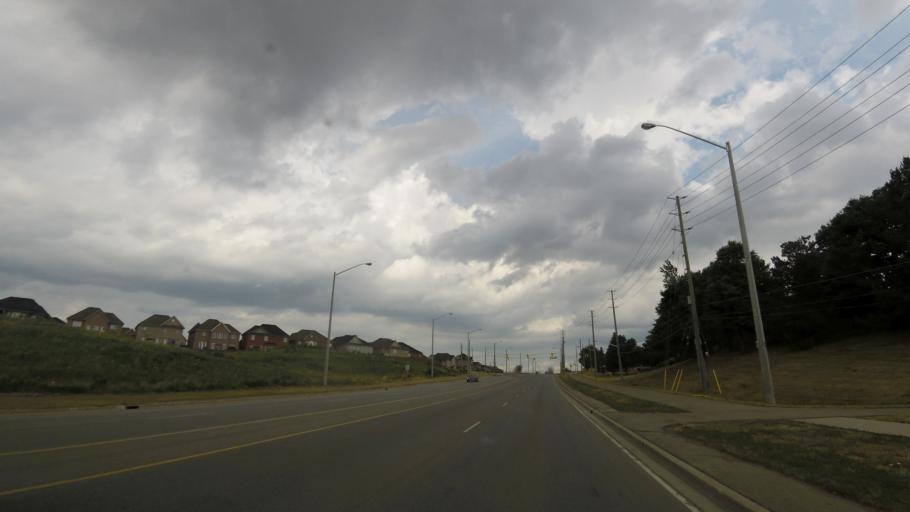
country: CA
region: Ontario
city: Brampton
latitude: 43.7392
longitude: -79.8196
